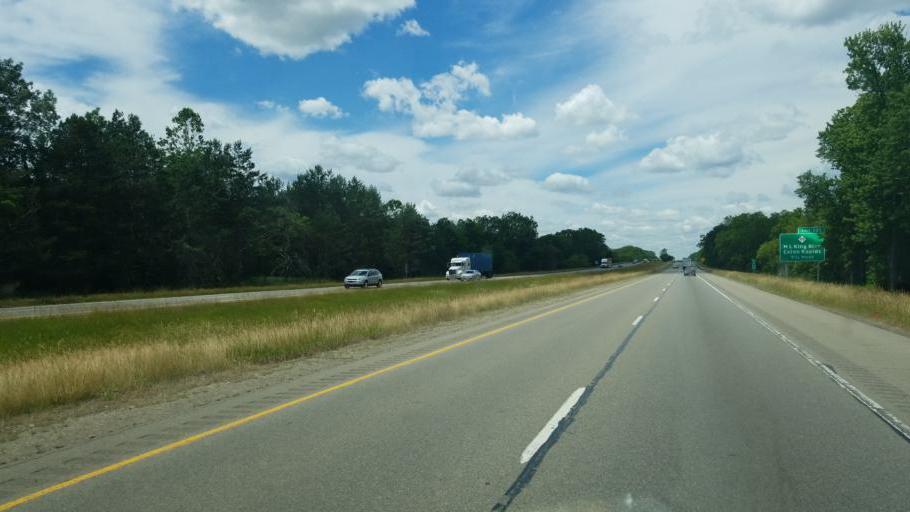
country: US
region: Michigan
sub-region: Ingham County
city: Holt
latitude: 42.6600
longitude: -84.5570
